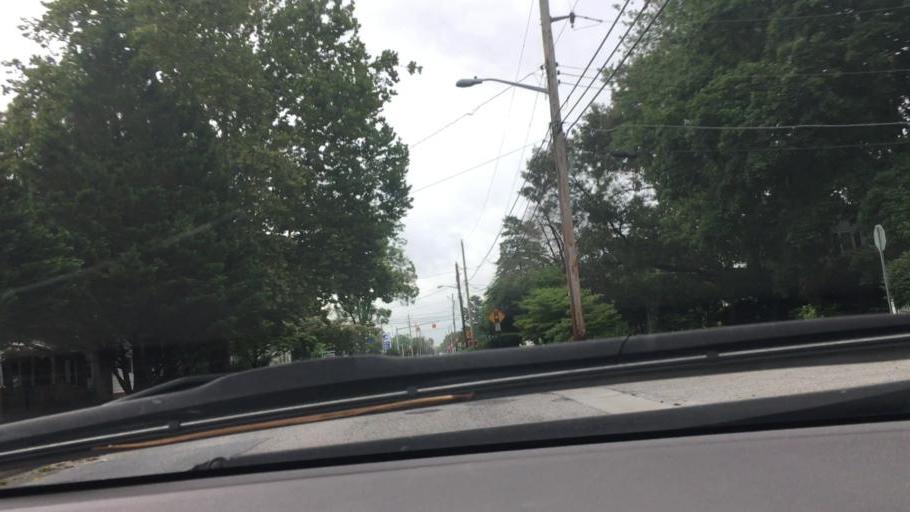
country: US
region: Maryland
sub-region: Wicomico County
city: Fruitland
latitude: 38.3292
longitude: -75.6246
